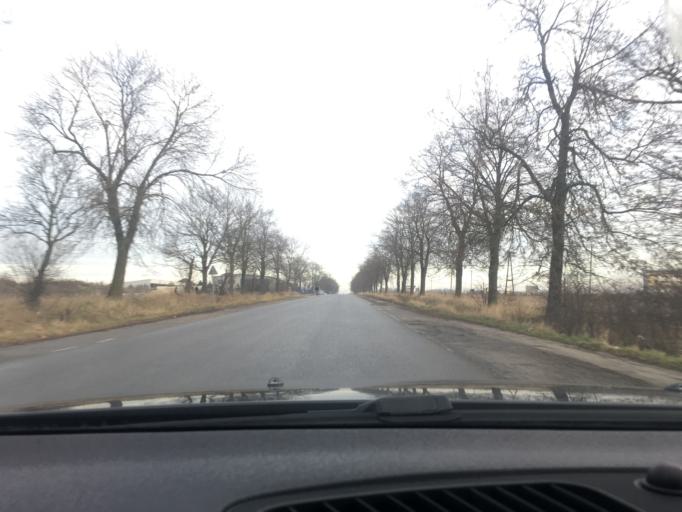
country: PL
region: Swietokrzyskie
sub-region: Powiat jedrzejowski
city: Jedrzejow
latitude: 50.6495
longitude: 20.3175
